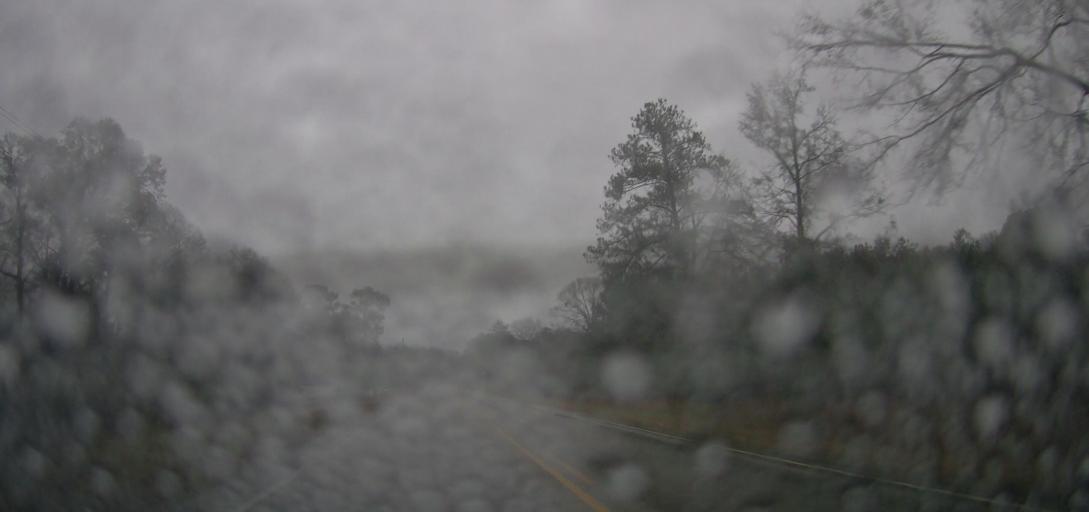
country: US
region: Alabama
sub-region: Autauga County
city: Prattville
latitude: 32.5162
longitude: -86.5955
